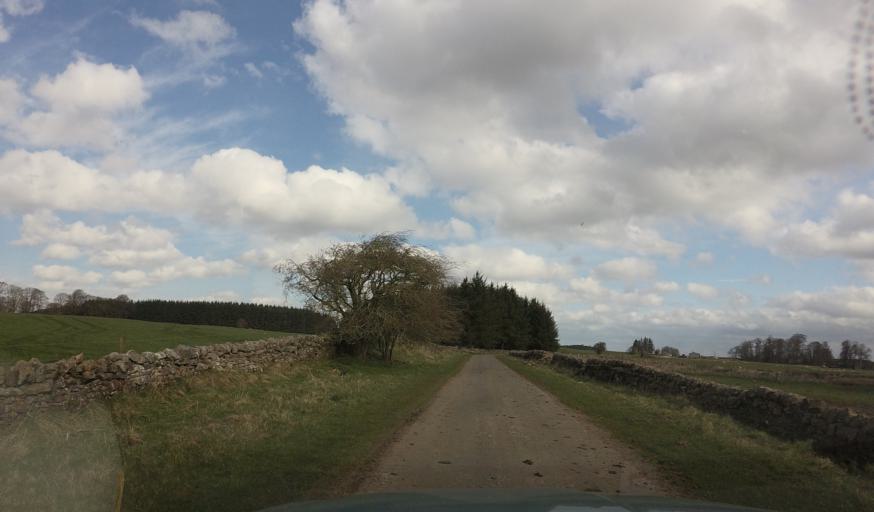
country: GB
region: Scotland
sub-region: Midlothian
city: Penicuik
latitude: 55.7962
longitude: -3.1673
